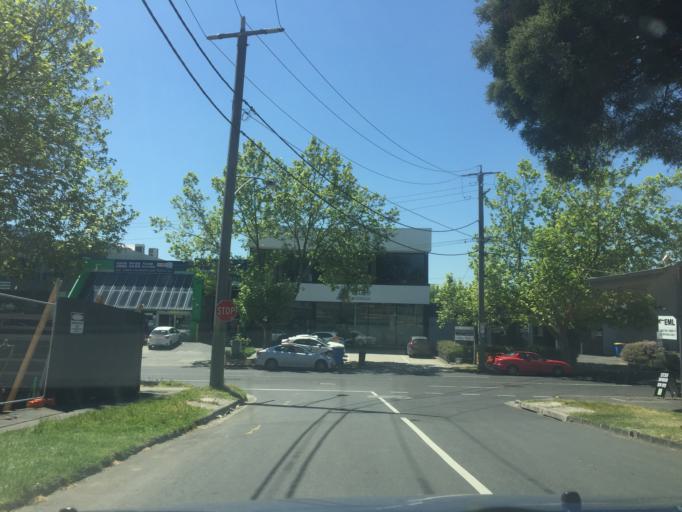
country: AU
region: Victoria
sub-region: Boroondara
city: Canterbury
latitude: -37.8254
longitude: 145.0901
